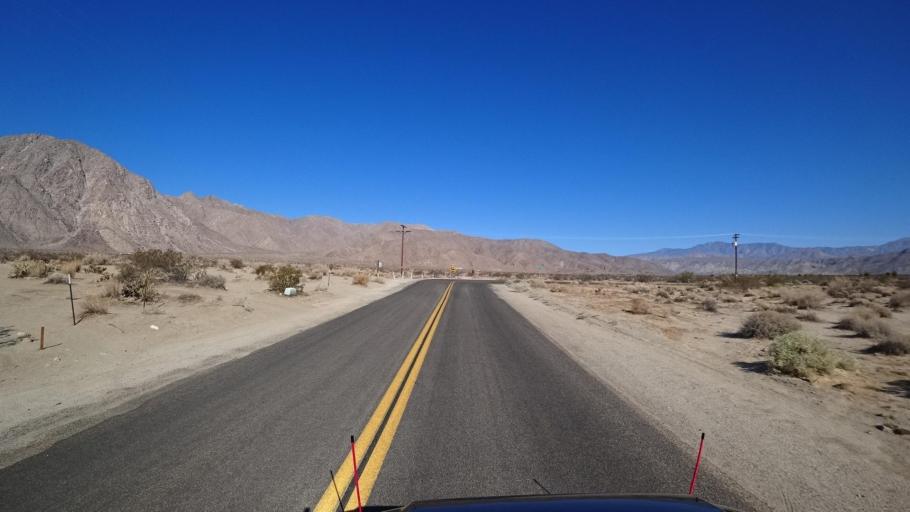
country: US
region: California
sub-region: San Diego County
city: Borrego Springs
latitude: 33.3002
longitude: -116.3868
